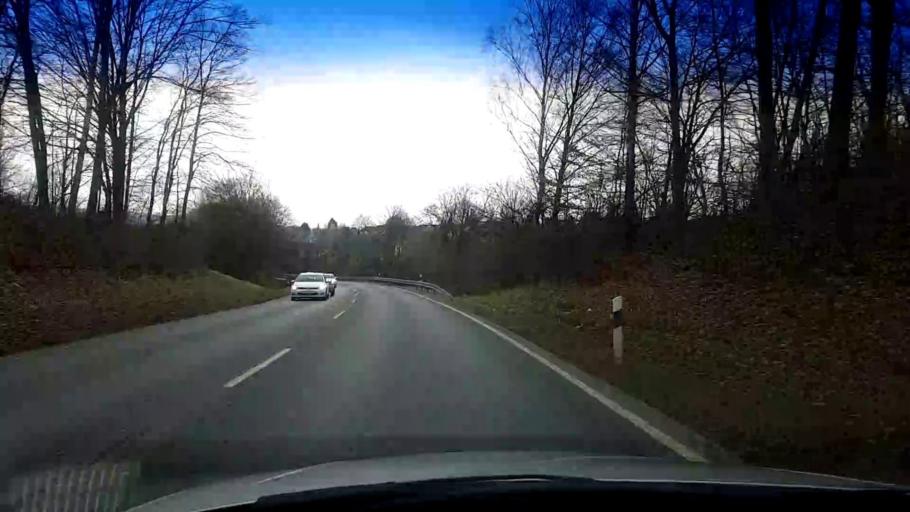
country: DE
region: Bavaria
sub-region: Upper Franconia
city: Kulmbach
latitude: 50.0924
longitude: 11.4525
